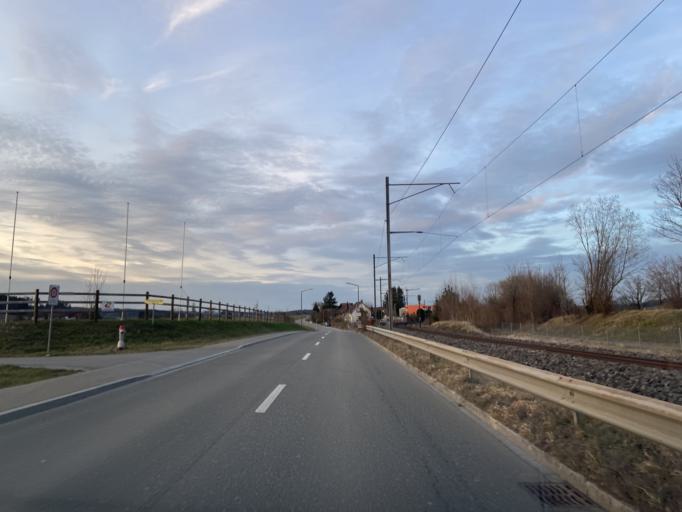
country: CH
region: Zurich
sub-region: Bezirk Winterthur
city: Wuelflingen (Kreis 6) / Lindenplatz
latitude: 47.5191
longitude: 8.6953
